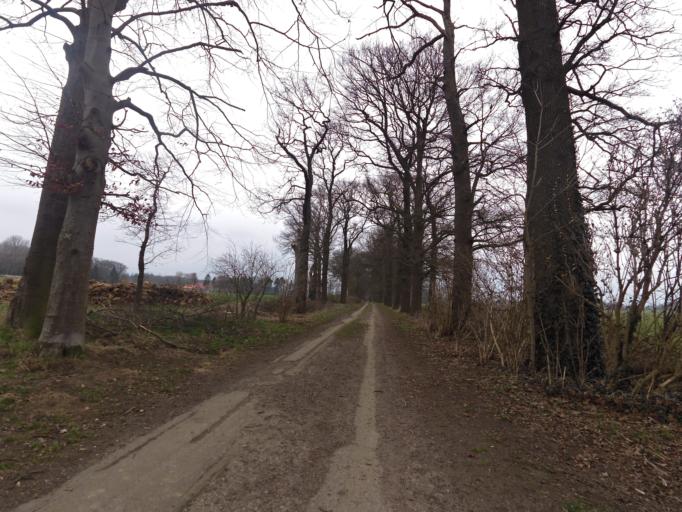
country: DE
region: North Rhine-Westphalia
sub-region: Regierungsbezirk Munster
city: Isselburg
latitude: 51.8579
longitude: 6.4314
